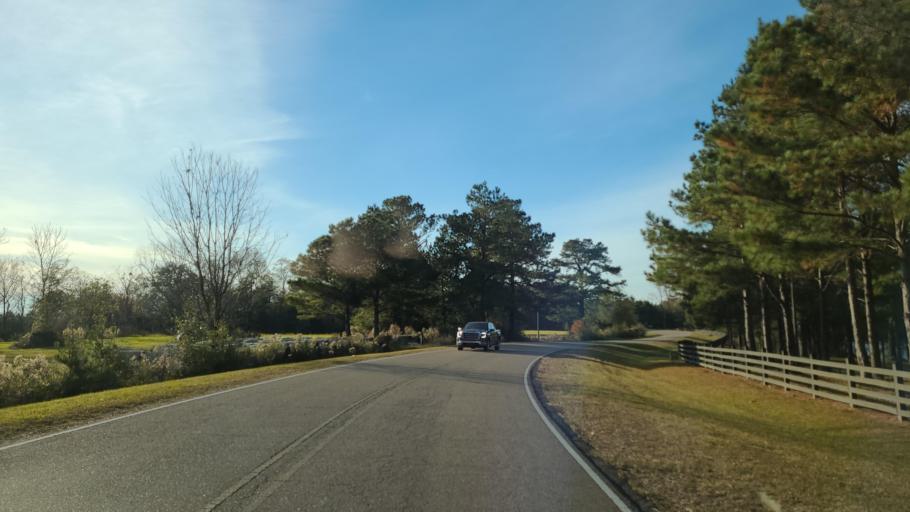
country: US
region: Mississippi
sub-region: Lamar County
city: Purvis
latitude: 31.1653
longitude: -89.3166
